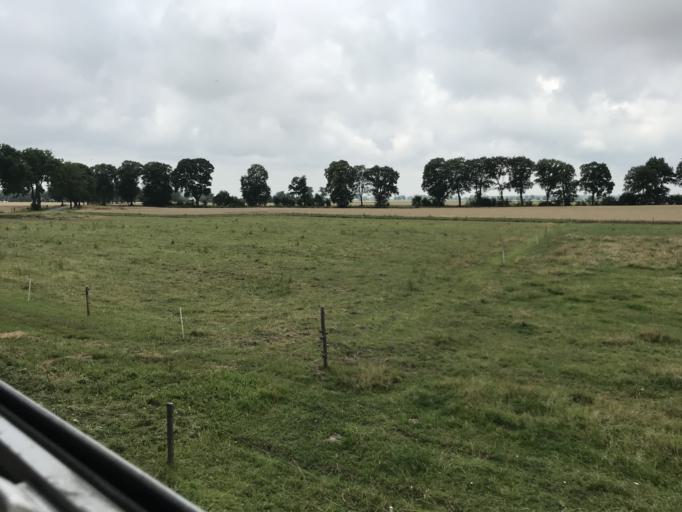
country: PL
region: Pomeranian Voivodeship
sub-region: Powiat malborski
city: Stare Pole
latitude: 54.0583
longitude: 19.2253
